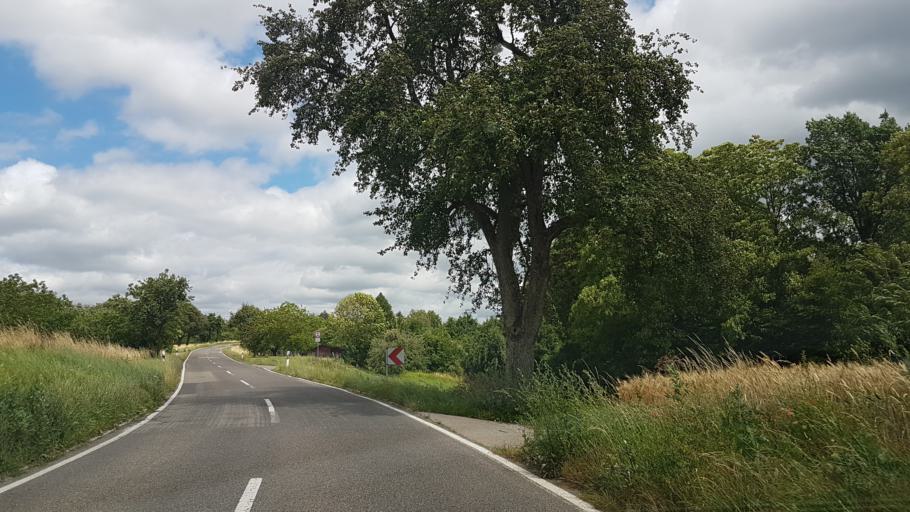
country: DE
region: Baden-Wuerttemberg
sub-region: Regierungsbezirk Stuttgart
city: Ittlingen
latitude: 49.2434
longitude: 8.9348
